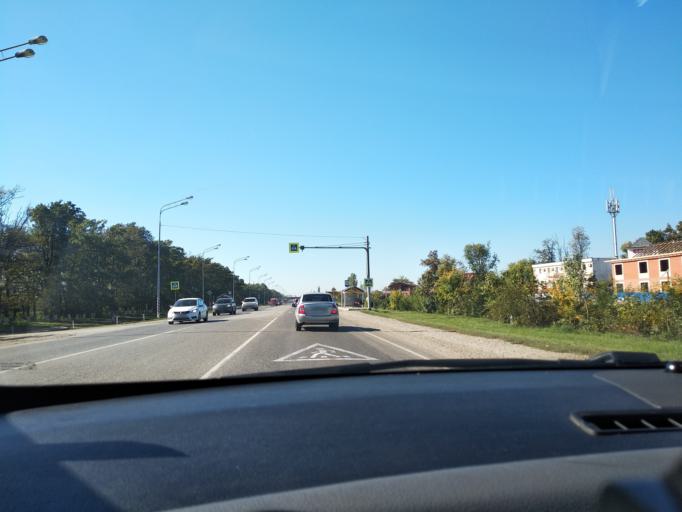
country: RU
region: Krasnodarskiy
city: Novotitarovskaya
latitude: 45.1402
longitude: 39.0381
